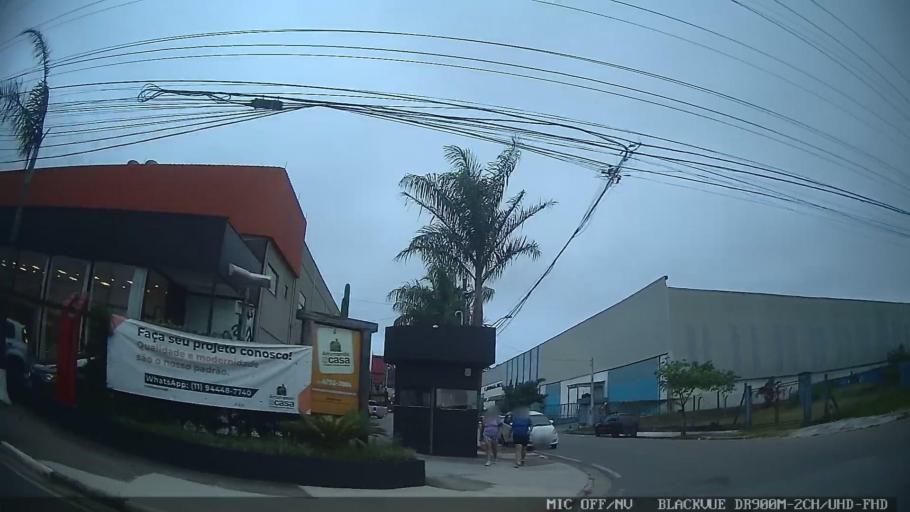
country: BR
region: Sao Paulo
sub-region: Mogi das Cruzes
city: Mogi das Cruzes
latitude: -23.5168
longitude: -46.1551
